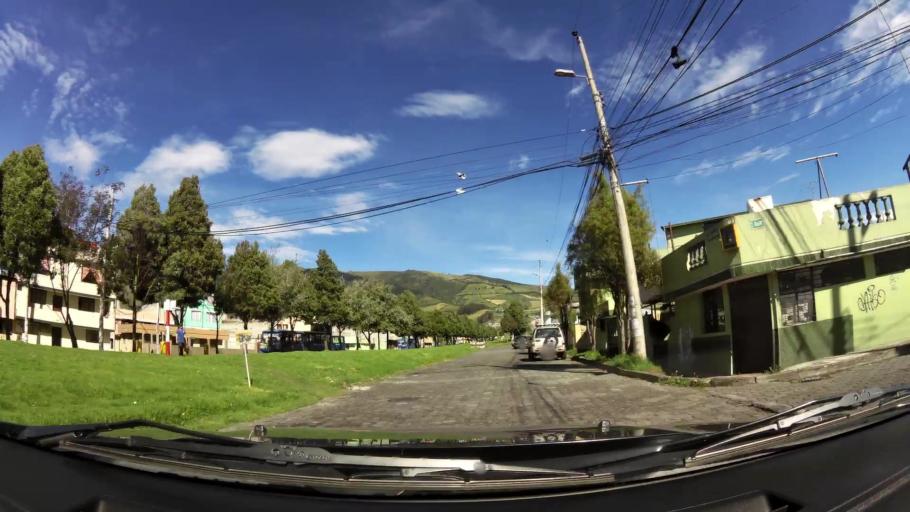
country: EC
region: Pichincha
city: Quito
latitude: -0.2912
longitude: -78.5637
